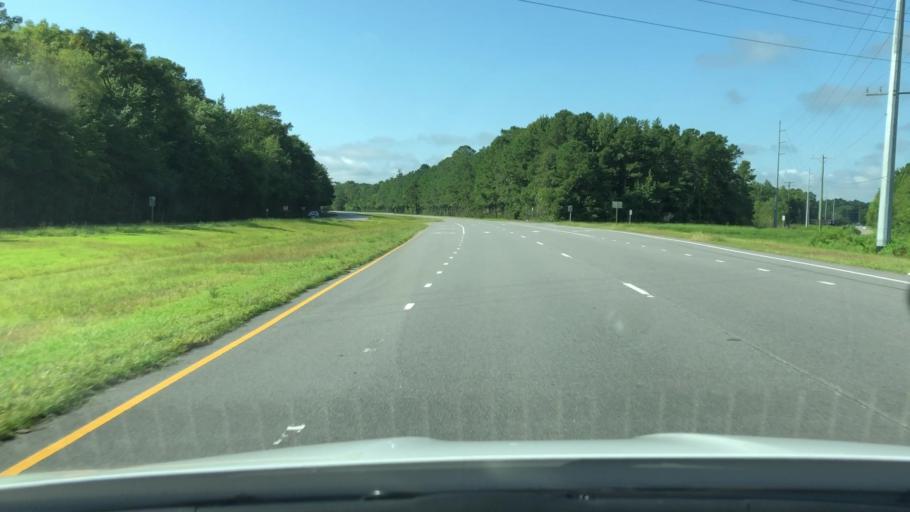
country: US
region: North Carolina
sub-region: Pasquotank County
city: Elizabeth City
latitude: 36.4278
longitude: -76.3420
